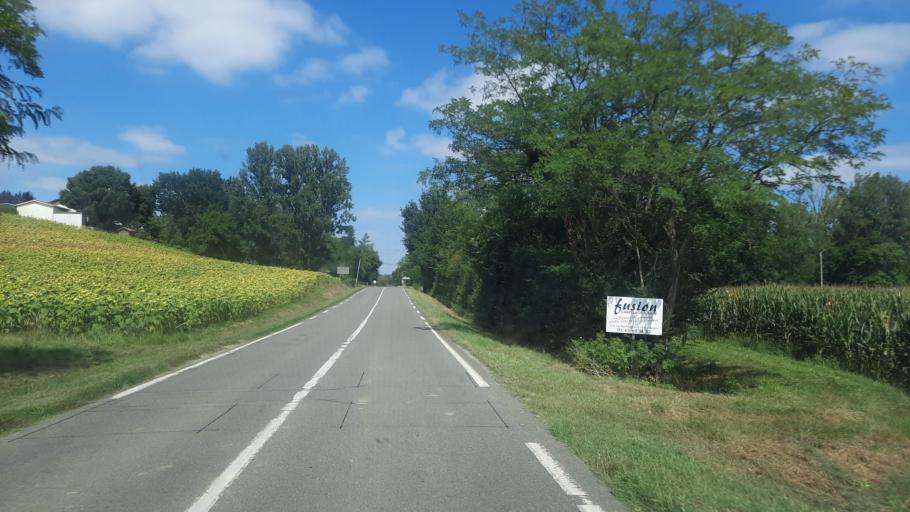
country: FR
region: Midi-Pyrenees
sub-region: Departement du Gers
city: Lombez
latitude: 43.4348
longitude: 0.8469
